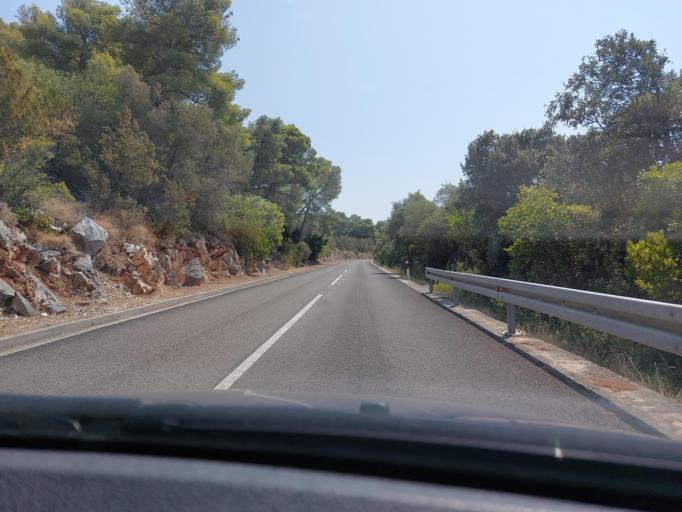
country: HR
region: Dubrovacko-Neretvanska
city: Smokvica
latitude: 42.7685
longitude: 16.8754
